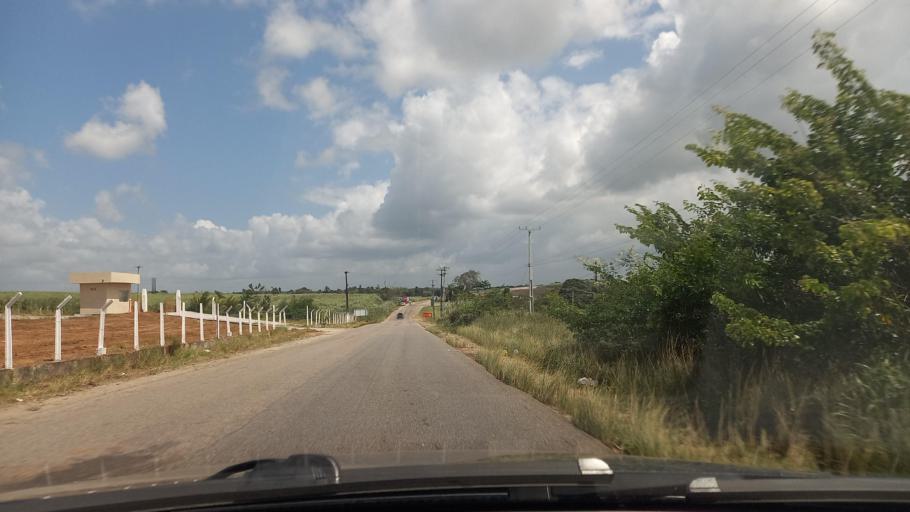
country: BR
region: Pernambuco
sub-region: Goiana
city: Goiana
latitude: -7.5579
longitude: -35.0329
